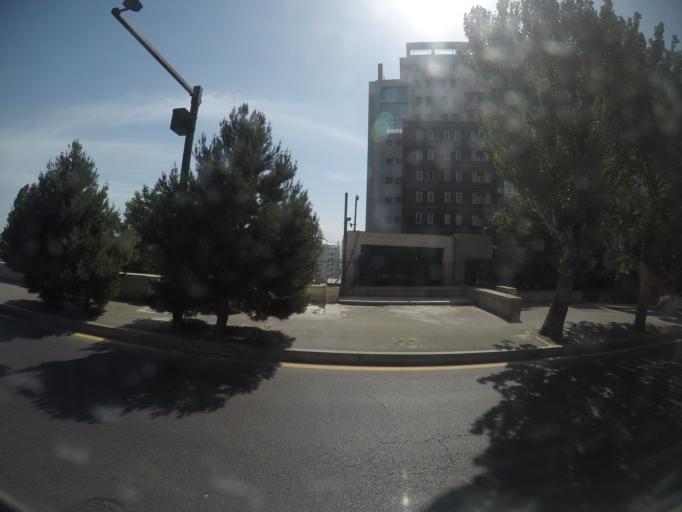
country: AZ
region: Baki
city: Badamdar
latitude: 40.3673
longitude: 49.8249
